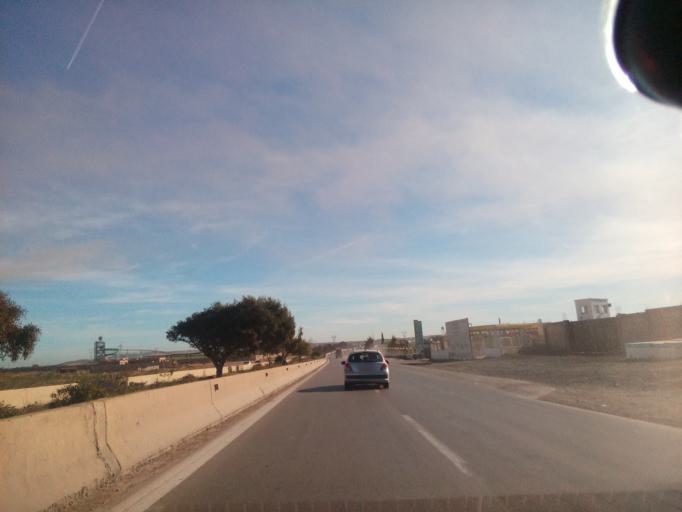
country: DZ
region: Oran
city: Ain el Bya
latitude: 35.7801
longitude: -0.2744
